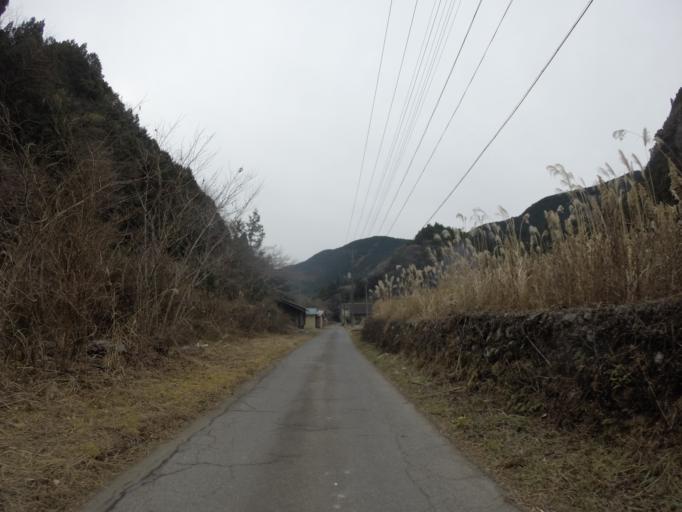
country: JP
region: Shizuoka
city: Fujinomiya
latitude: 35.2807
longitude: 138.5324
